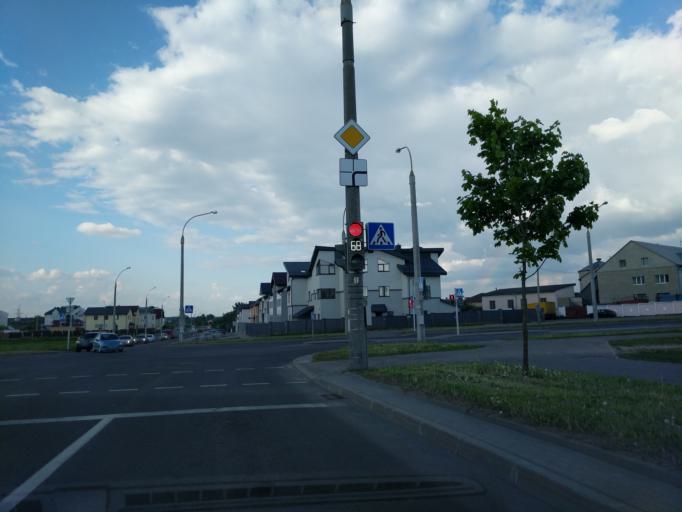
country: BY
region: Minsk
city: Zhdanovichy
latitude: 53.9353
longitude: 27.4317
